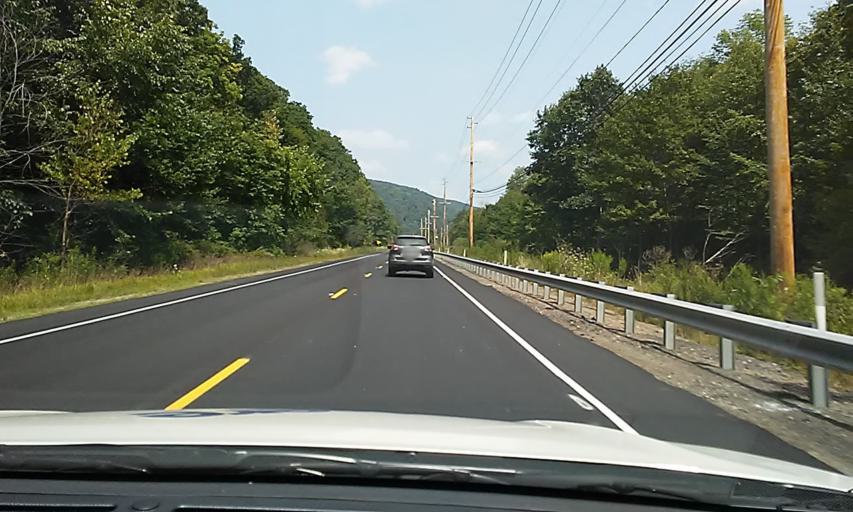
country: US
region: Pennsylvania
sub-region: Cameron County
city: Emporium
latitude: 41.4747
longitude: -78.3285
